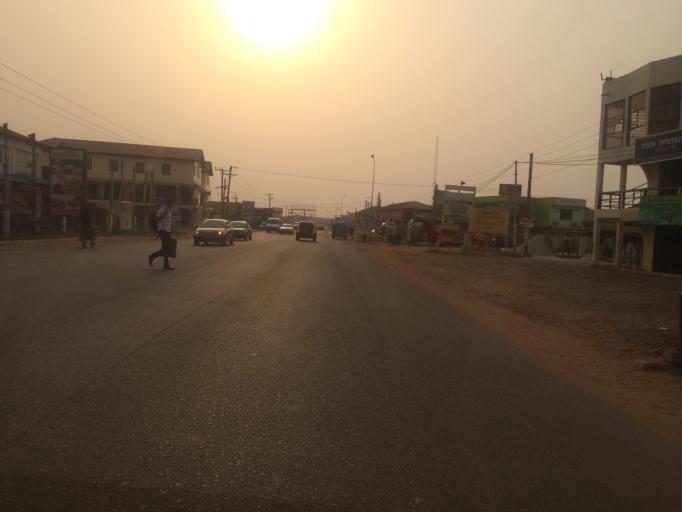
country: GH
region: Greater Accra
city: Nungua
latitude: 5.6345
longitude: -0.0994
